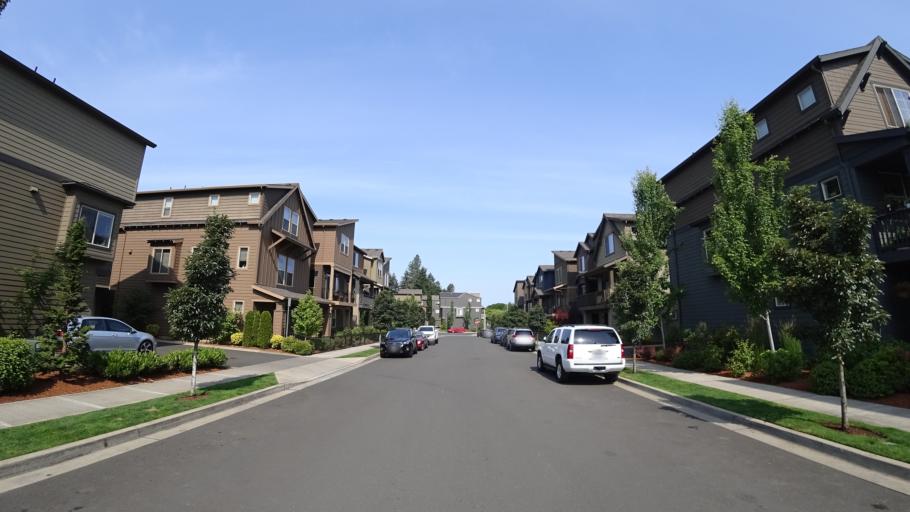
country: US
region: Oregon
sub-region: Washington County
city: Cedar Mill
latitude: 45.5057
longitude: -122.8234
